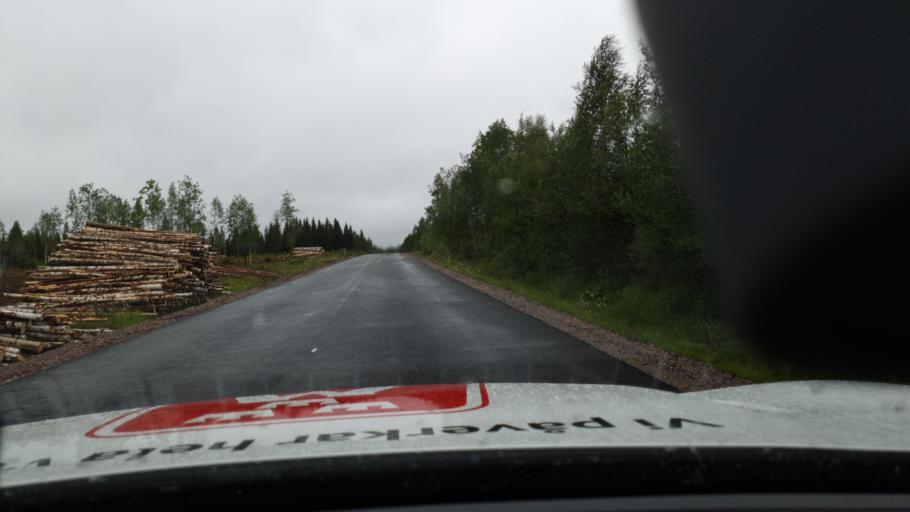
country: SE
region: Norrbotten
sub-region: Overtornea Kommun
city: OEvertornea
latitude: 66.5365
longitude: 23.3627
